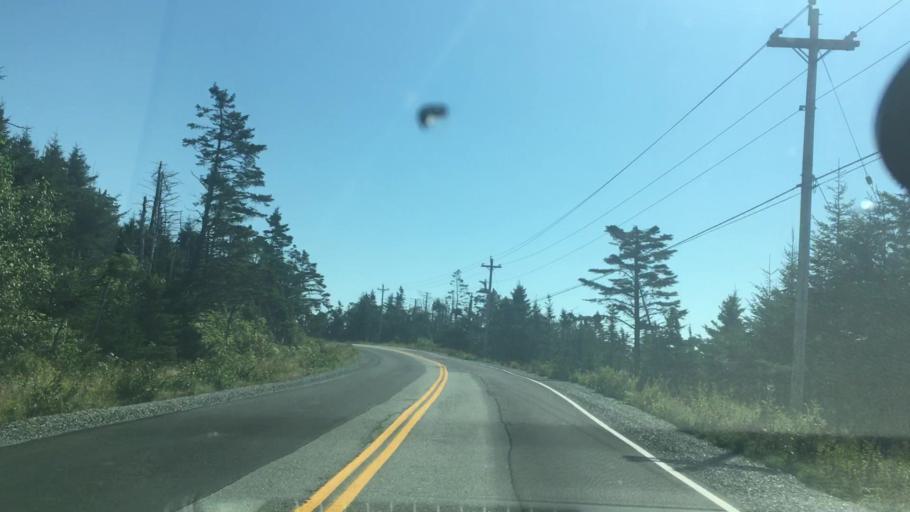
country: CA
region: Nova Scotia
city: New Glasgow
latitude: 44.9162
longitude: -62.3191
